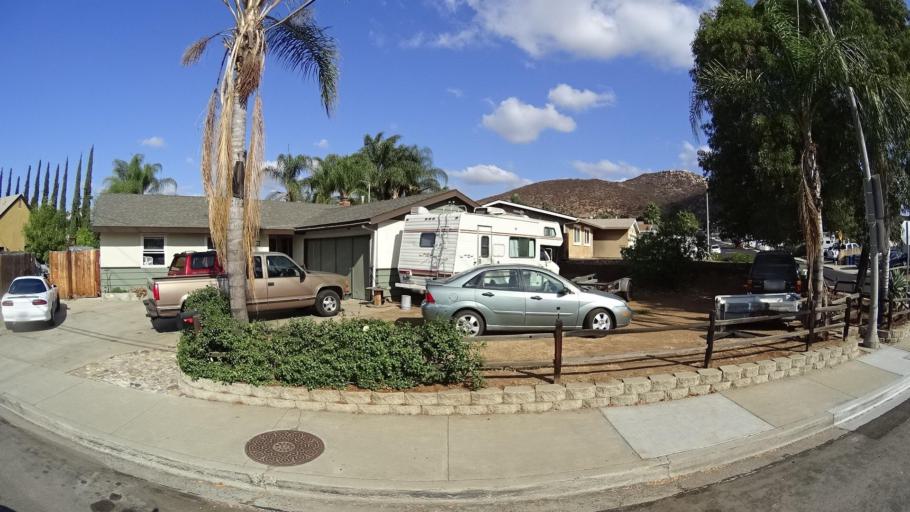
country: US
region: California
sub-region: San Diego County
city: Eucalyptus Hills
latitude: 32.8635
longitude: -116.9629
